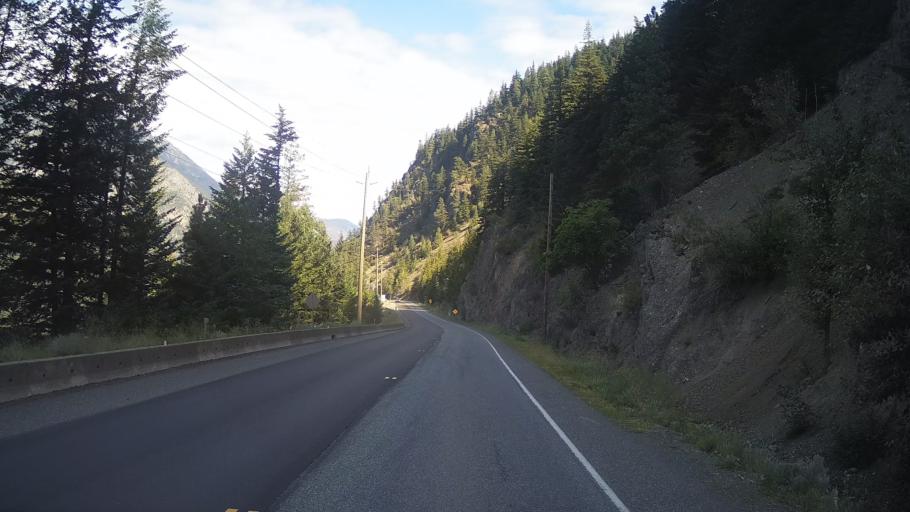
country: CA
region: British Columbia
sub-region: Thompson-Nicola Regional District
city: Ashcroft
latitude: 50.0798
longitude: -121.5514
